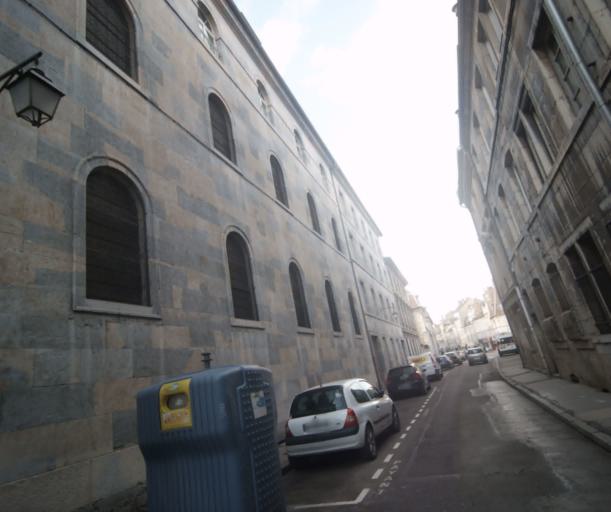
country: FR
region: Franche-Comte
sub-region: Departement du Doubs
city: Besancon
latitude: 47.2356
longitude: 6.0297
